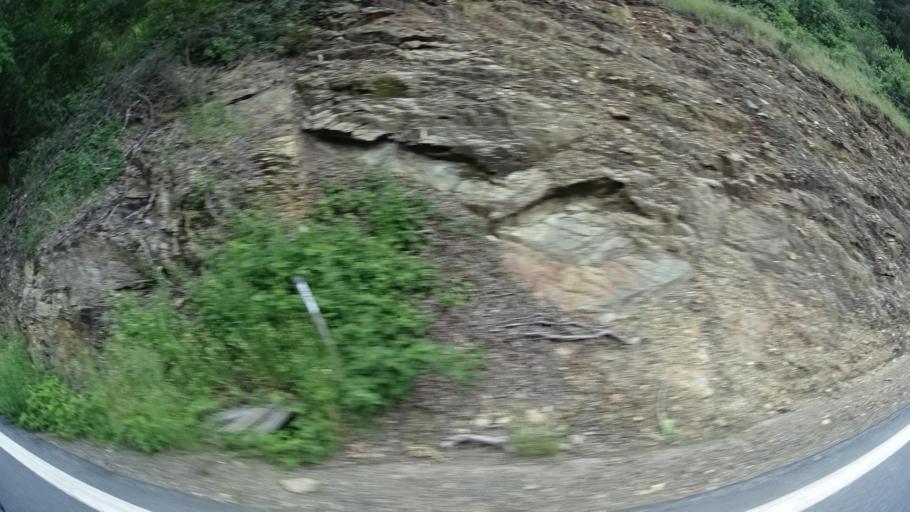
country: US
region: California
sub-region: Humboldt County
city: Willow Creek
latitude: 41.1122
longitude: -123.6865
